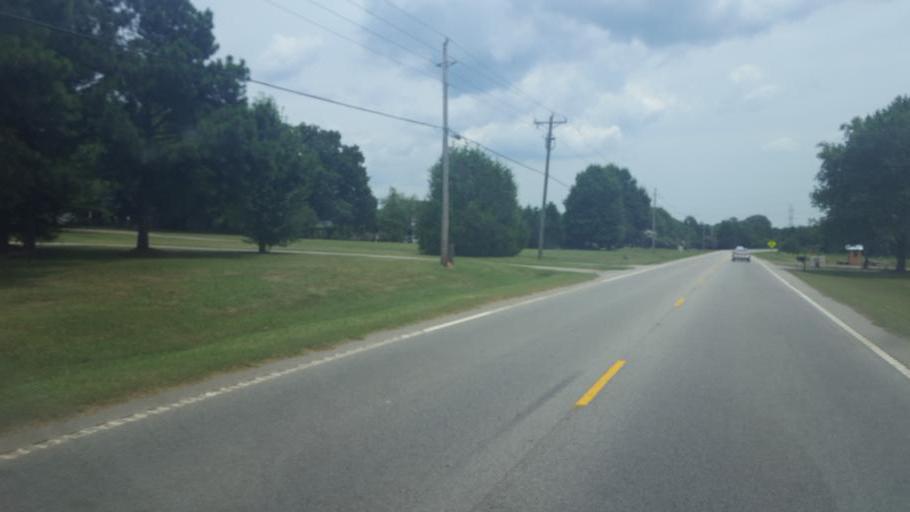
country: US
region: South Carolina
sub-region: York County
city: Newport
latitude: 34.9630
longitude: -81.1435
